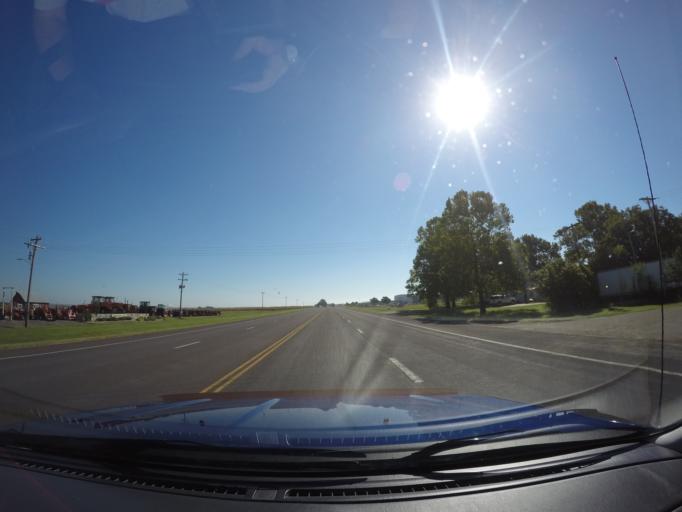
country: US
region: Kansas
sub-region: Pottawatomie County
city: Wamego
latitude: 39.2100
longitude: -96.2922
